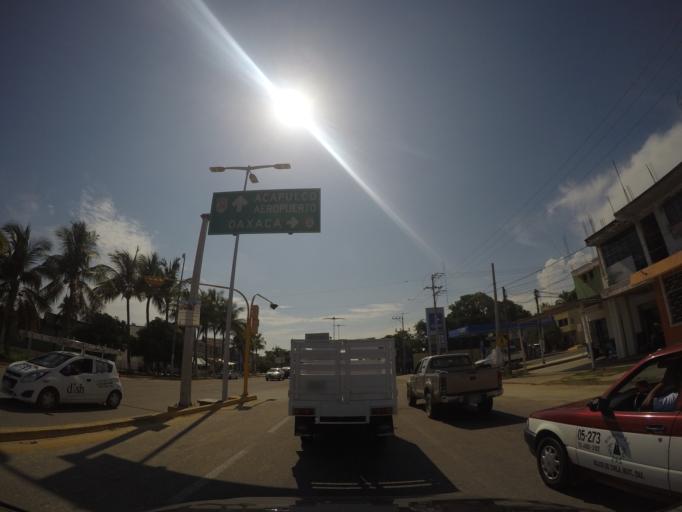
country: MX
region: Oaxaca
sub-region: San Pedro Mixtepec -Dto. 22 -
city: Puerto Escondido
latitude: 15.8675
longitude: -97.0797
